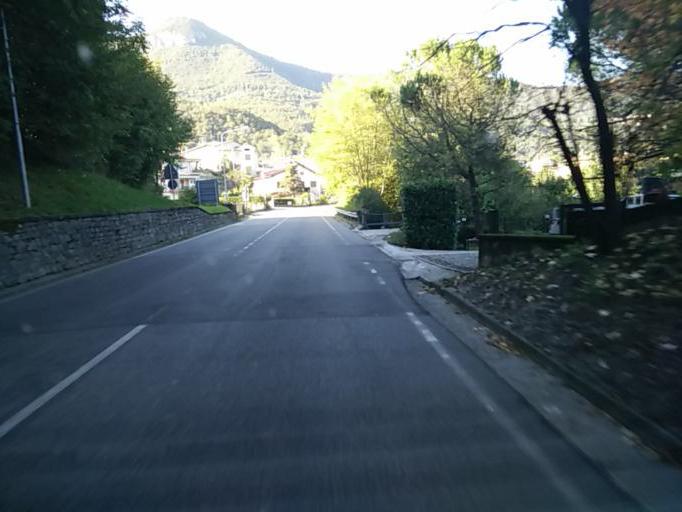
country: IT
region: Lombardy
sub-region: Provincia di Brescia
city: Roe Volciano
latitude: 45.6079
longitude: 10.4826
